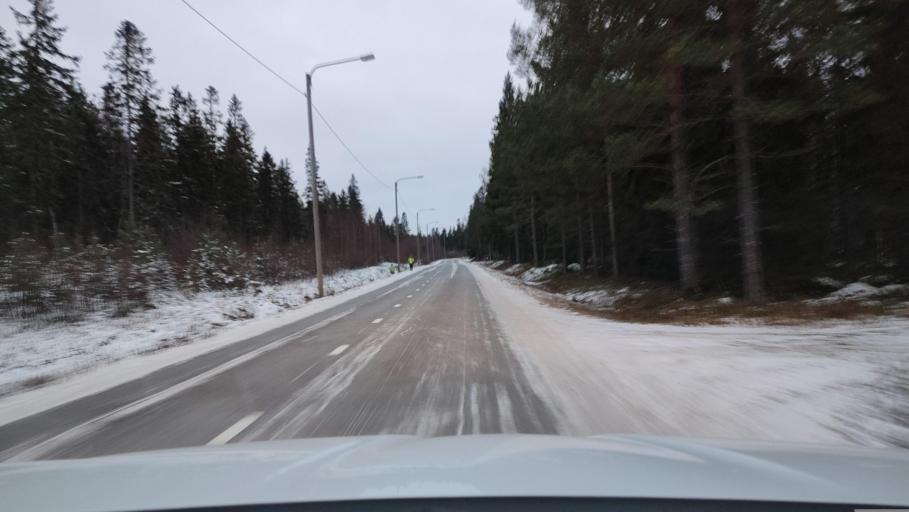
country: FI
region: Ostrobothnia
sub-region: Vaasa
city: Replot
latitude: 63.3584
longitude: 21.3031
